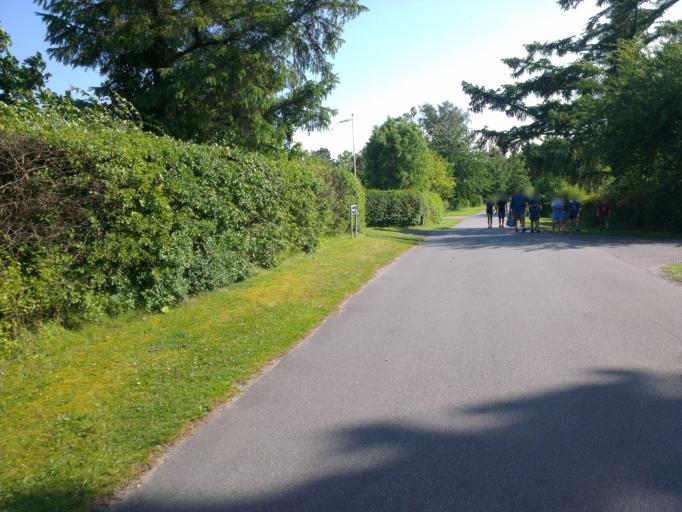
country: DK
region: Capital Region
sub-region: Halsnaes Kommune
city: Hundested
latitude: 55.9332
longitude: 11.9206
